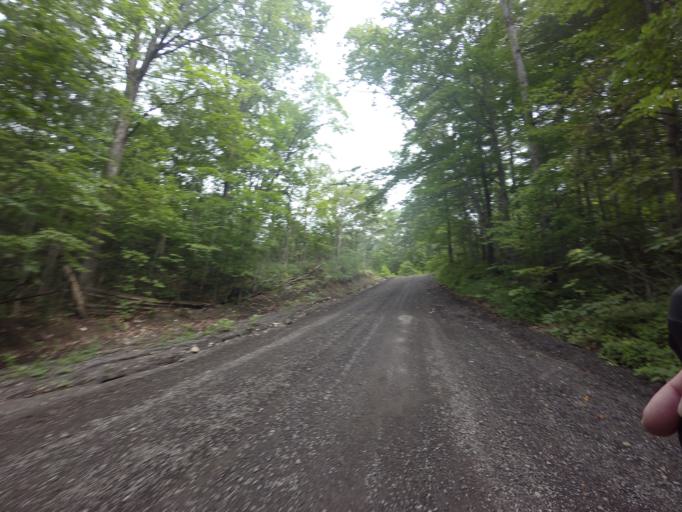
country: CA
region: Ontario
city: Kingston
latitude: 44.5624
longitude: -76.5763
